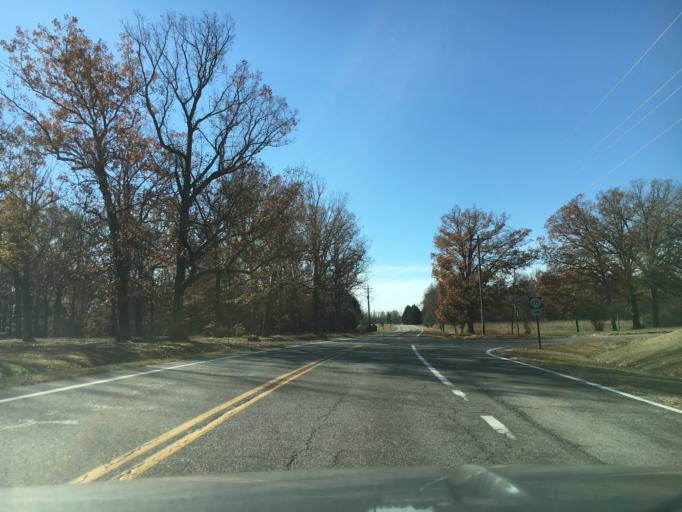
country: US
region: Virginia
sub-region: Cumberland County
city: Cumberland
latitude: 37.6029
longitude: -78.1678
